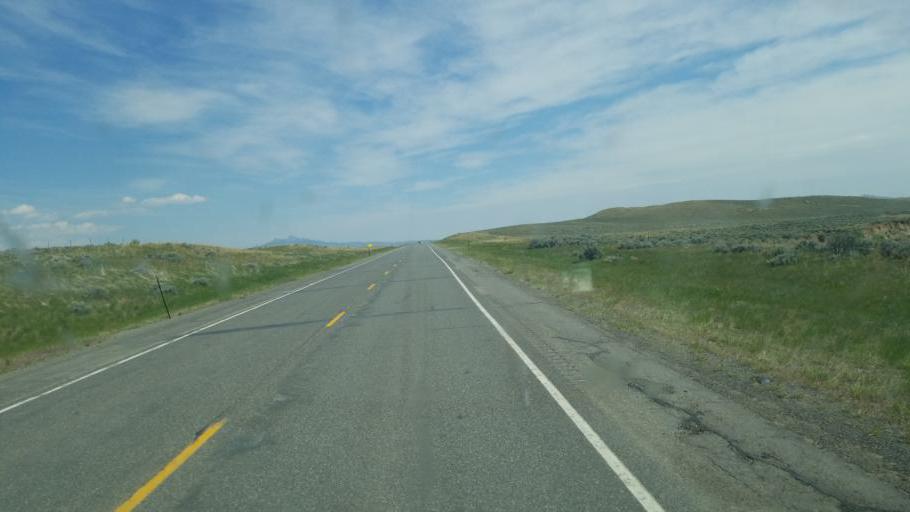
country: US
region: Wyoming
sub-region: Park County
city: Cody
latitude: 44.4263
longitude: -109.0107
